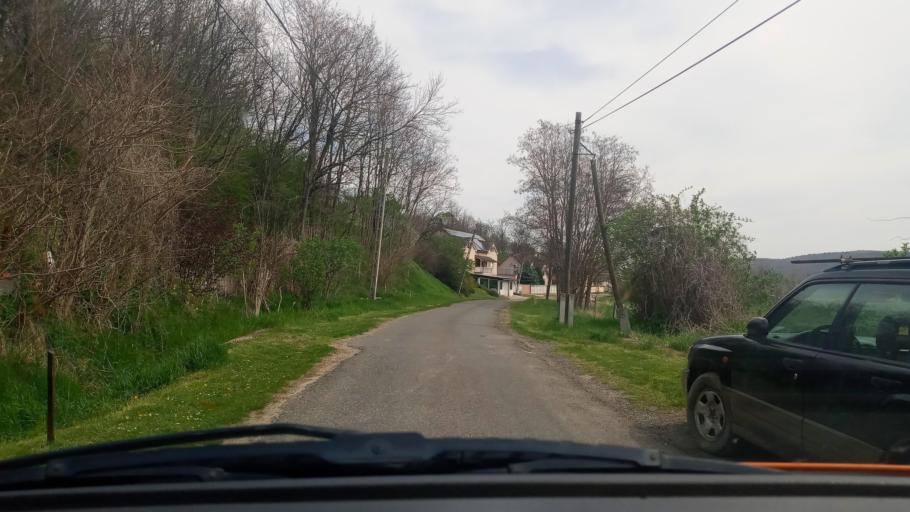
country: HU
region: Baranya
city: Hidas
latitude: 46.2515
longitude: 18.4831
